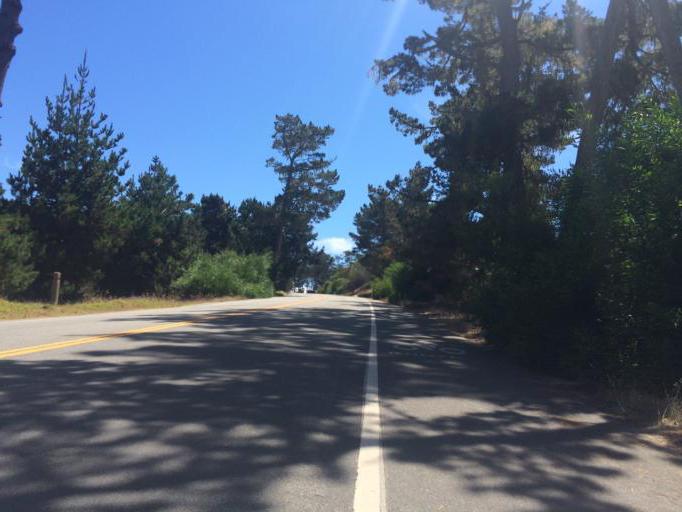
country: US
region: California
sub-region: Monterey County
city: Del Monte Forest
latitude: 36.5830
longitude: -121.9591
